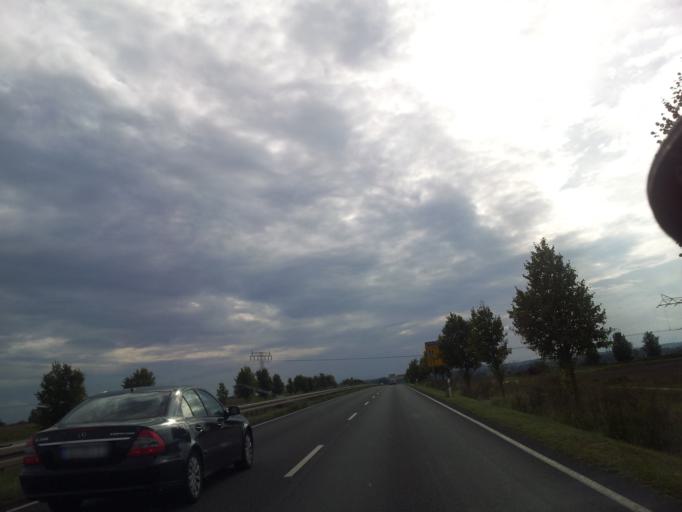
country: DE
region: Saxony-Anhalt
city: Wolmirstedt
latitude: 52.2590
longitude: 11.6122
